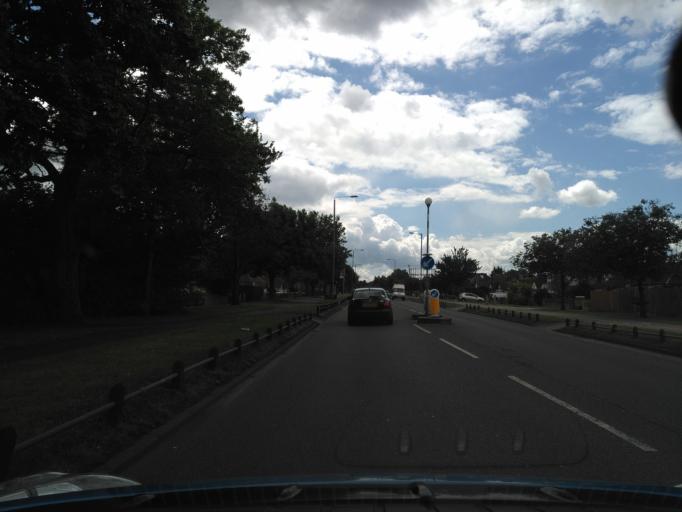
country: GB
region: England
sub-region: Greater London
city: Sidcup
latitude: 51.4061
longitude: 0.1132
